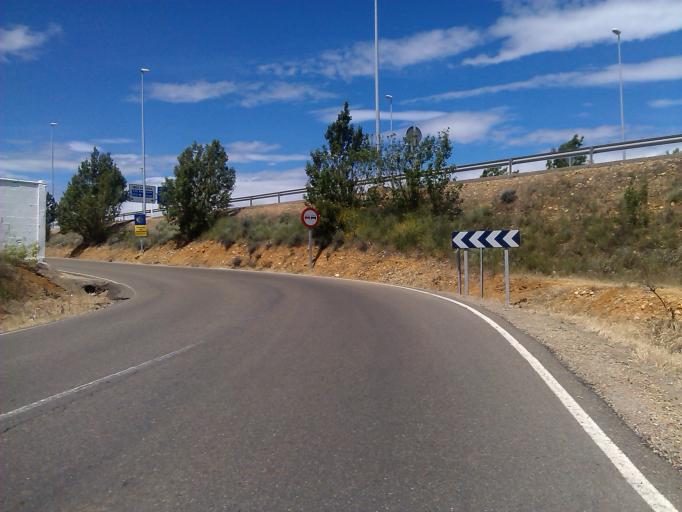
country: ES
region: Castille and Leon
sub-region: Provincia de Leon
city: Valverde de la Virgen
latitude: 42.5775
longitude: -5.6463
